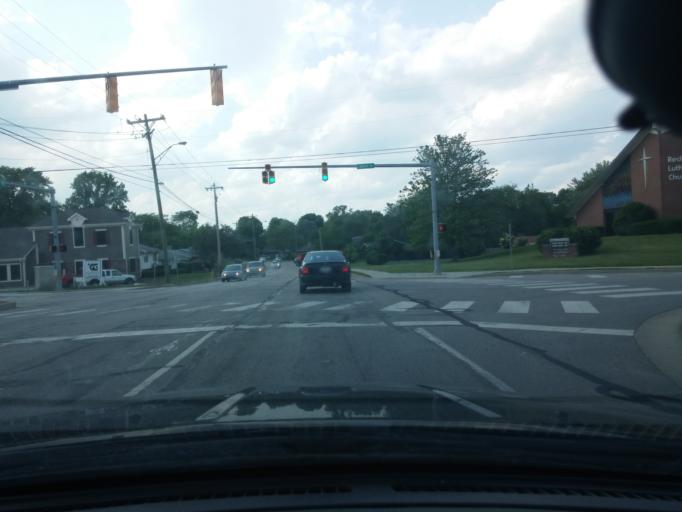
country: US
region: Indiana
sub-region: Tippecanoe County
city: West Lafayette
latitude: 40.4455
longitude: -86.9140
